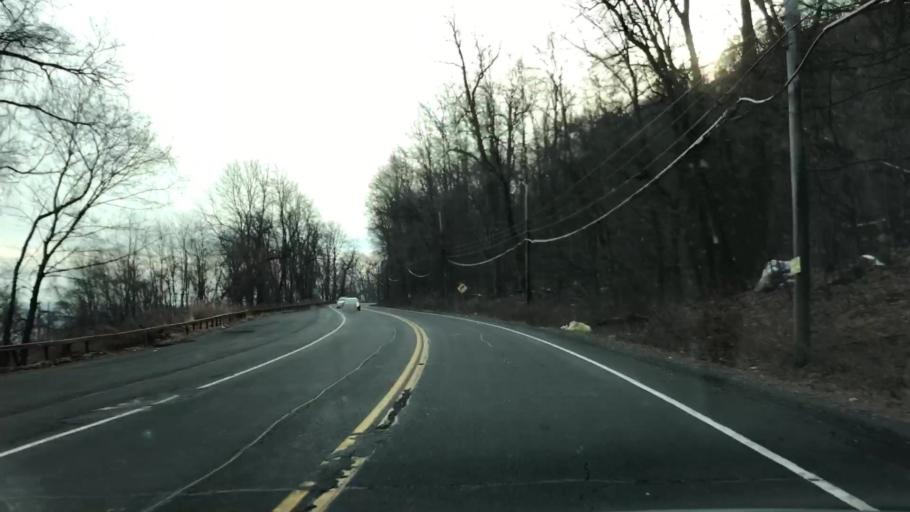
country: US
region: New York
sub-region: Rockland County
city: Haverstraw
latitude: 41.1796
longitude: -73.9497
